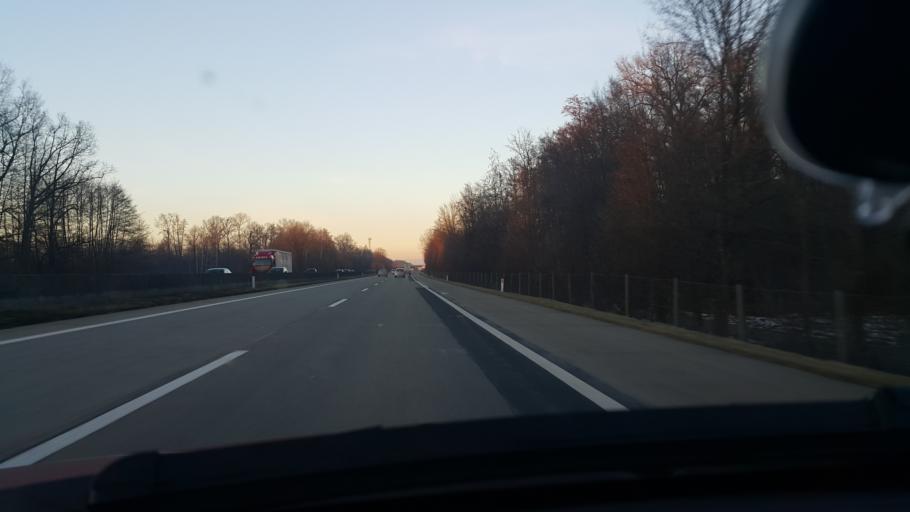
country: AT
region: Styria
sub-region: Politischer Bezirk Leibnitz
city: Gabersdorf
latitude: 46.7875
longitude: 15.5746
